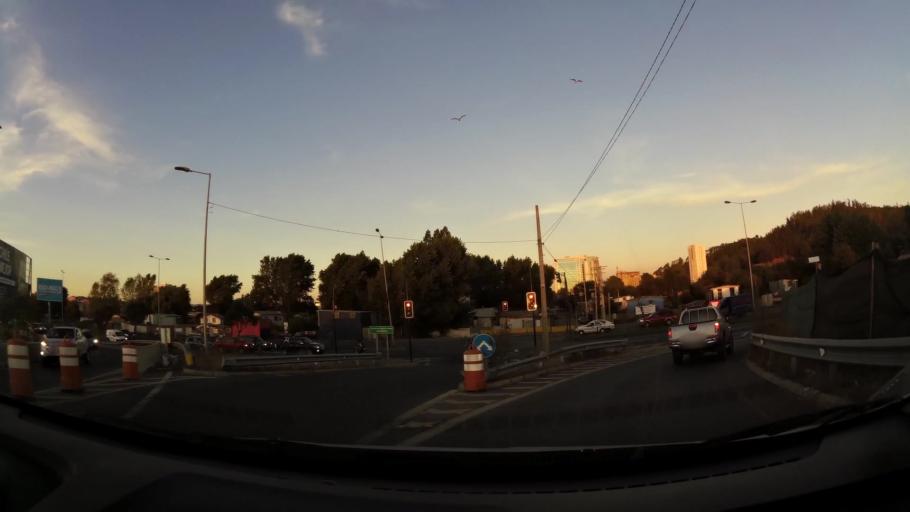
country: CL
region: Biobio
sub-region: Provincia de Concepcion
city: Concepcion
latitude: -36.8357
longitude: -73.0630
